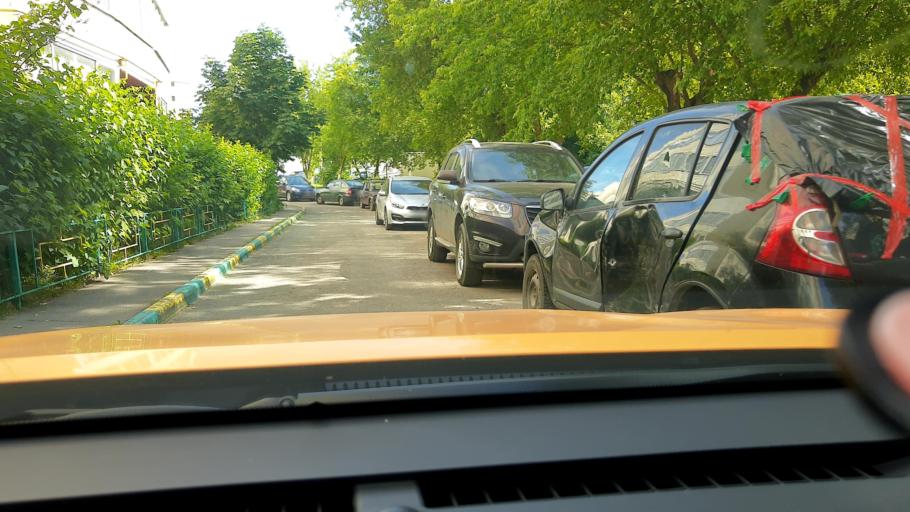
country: RU
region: Moskovskaya
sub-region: Podol'skiy Rayon
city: Podol'sk
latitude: 55.4115
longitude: 37.5454
